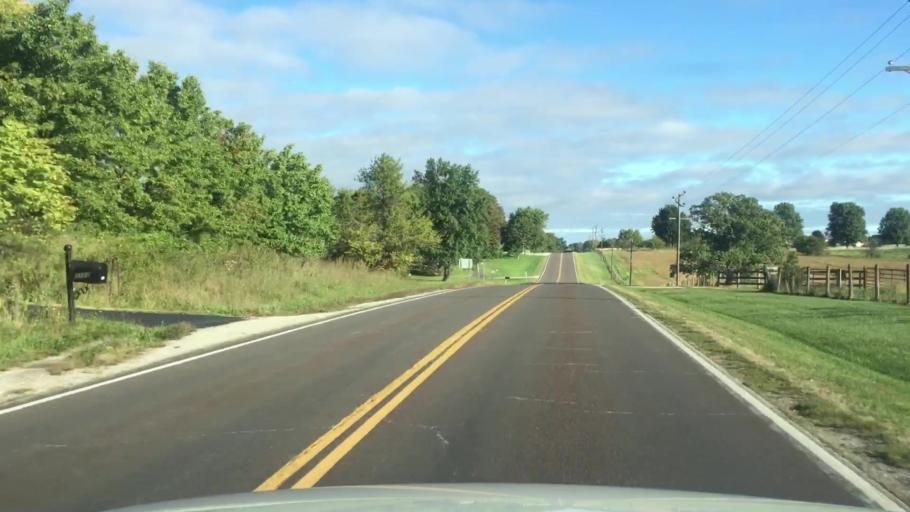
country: US
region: Missouri
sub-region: Howard County
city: New Franklin
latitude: 39.0430
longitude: -92.7444
